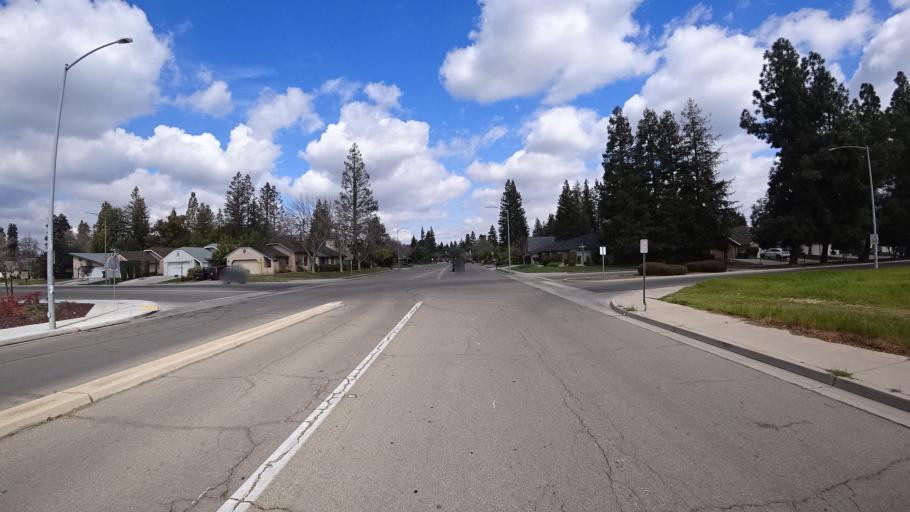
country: US
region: California
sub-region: Fresno County
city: Fresno
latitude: 36.8381
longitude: -119.8624
